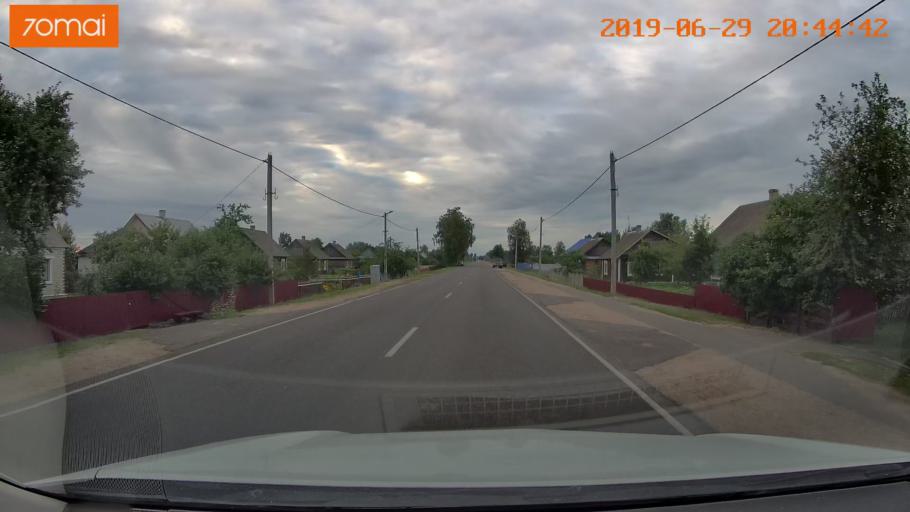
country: BY
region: Brest
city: Hantsavichy
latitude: 52.6162
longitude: 26.3074
